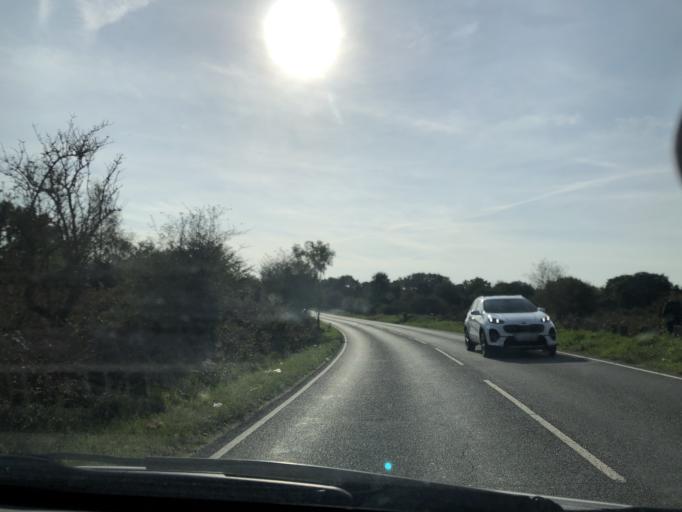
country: GB
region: England
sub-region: Kent
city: Dartford
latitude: 51.4350
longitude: 0.1918
